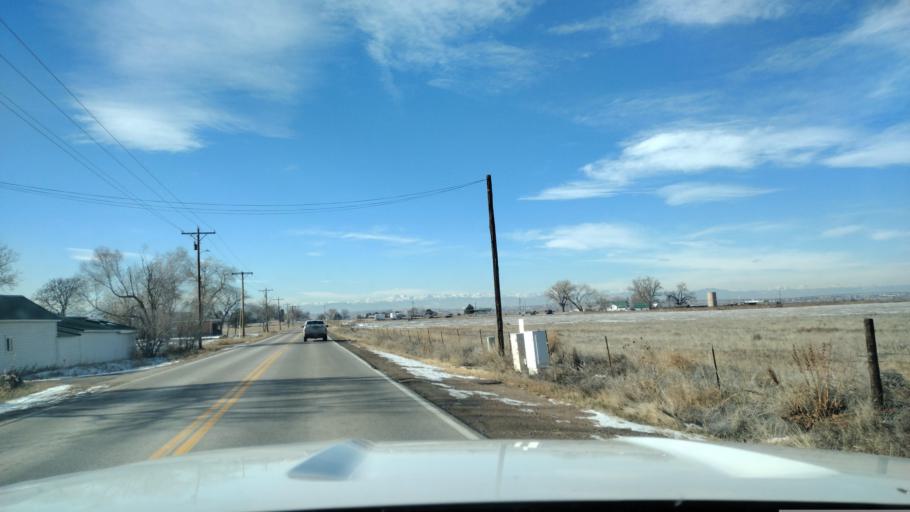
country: US
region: Colorado
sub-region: Adams County
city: Brighton
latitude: 39.9433
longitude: -104.8185
